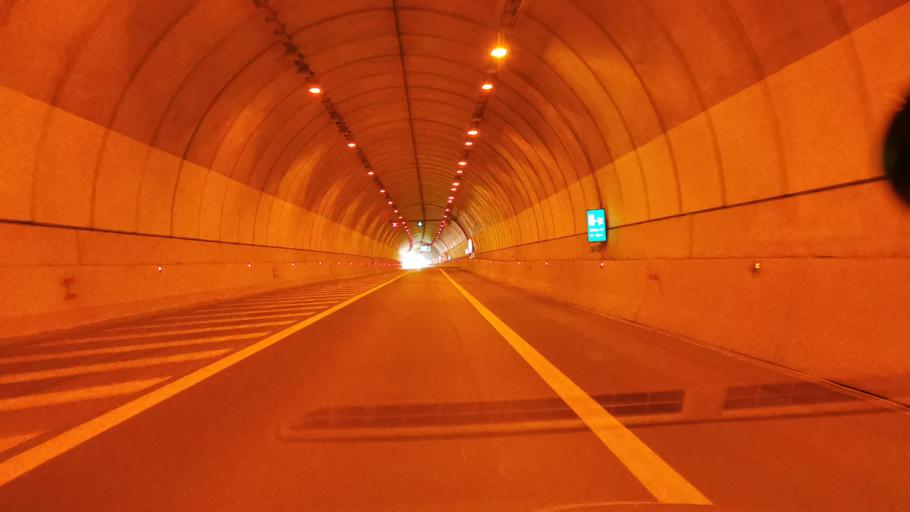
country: IT
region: Piedmont
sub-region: Provincia di Cuneo
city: Cuneo
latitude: 44.4268
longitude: 7.5679
